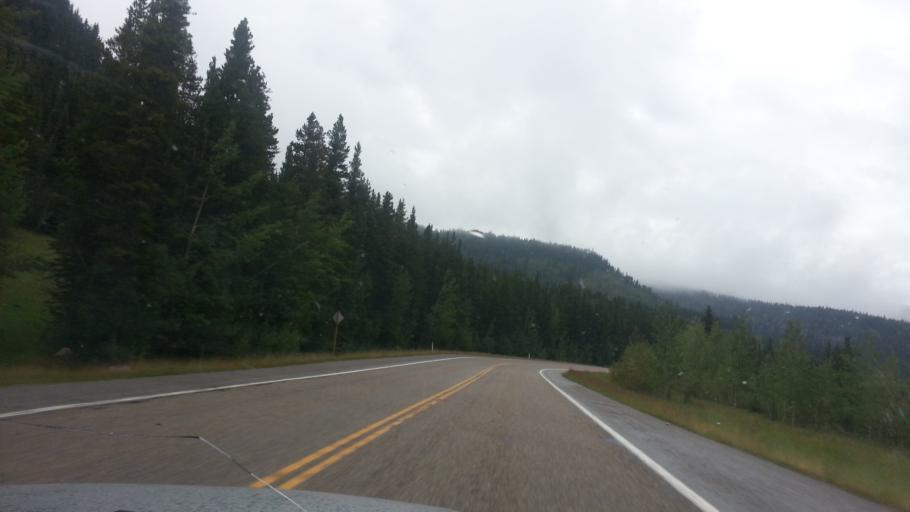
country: CA
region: Alberta
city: Cochrane
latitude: 50.8605
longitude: -114.7950
